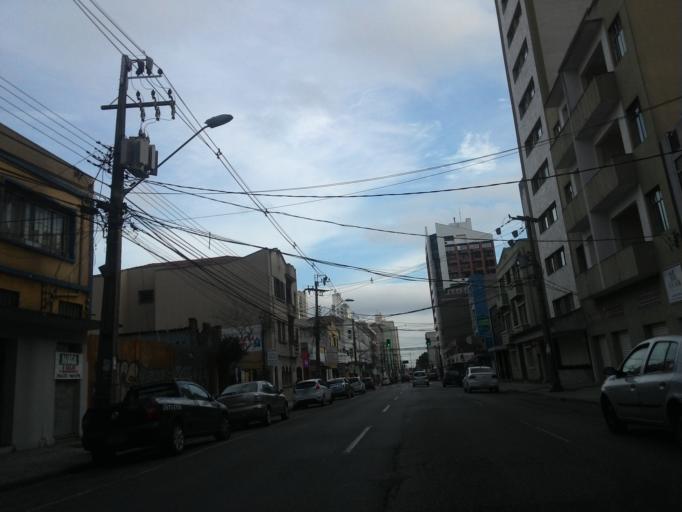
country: BR
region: Parana
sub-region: Curitiba
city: Curitiba
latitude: -25.4303
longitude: -49.2635
